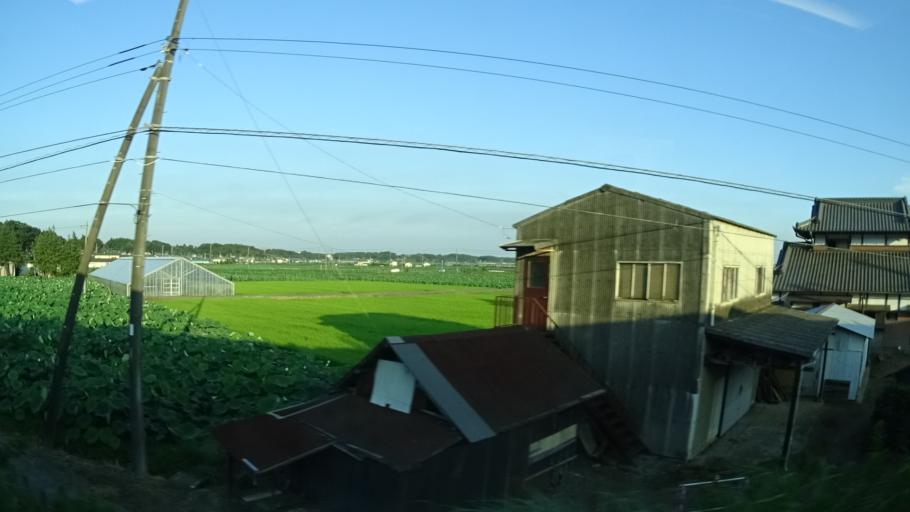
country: JP
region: Ibaraki
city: Ami
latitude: 36.0991
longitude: 140.2237
